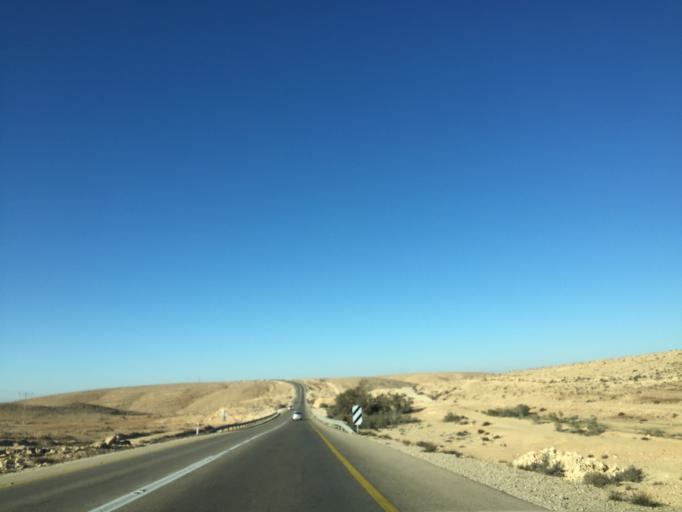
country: IL
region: Southern District
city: Mitzpe Ramon
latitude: 30.6681
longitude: 34.8048
